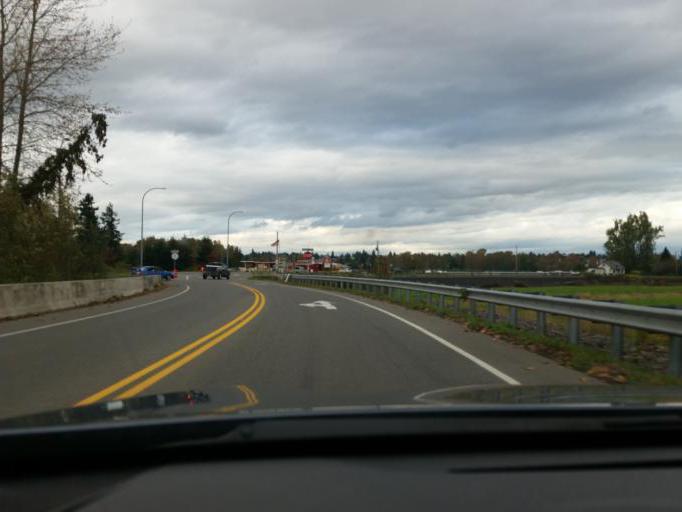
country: US
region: Washington
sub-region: Snohomish County
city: Snohomish
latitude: 47.8982
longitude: -122.1079
